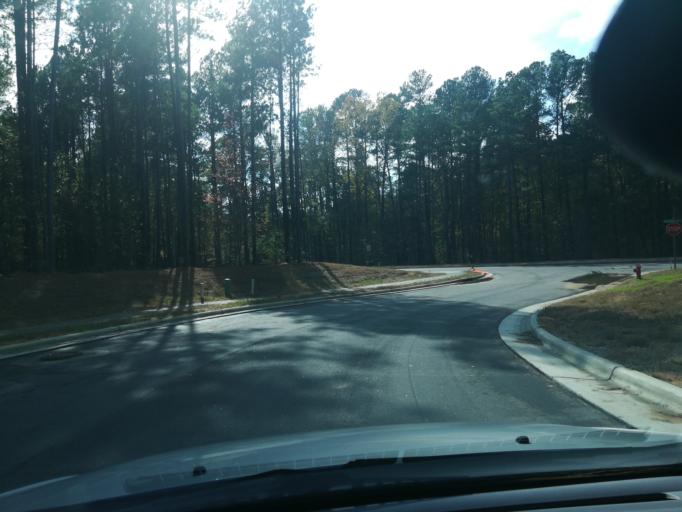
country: US
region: North Carolina
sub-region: Durham County
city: Durham
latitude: 36.0589
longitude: -78.9441
